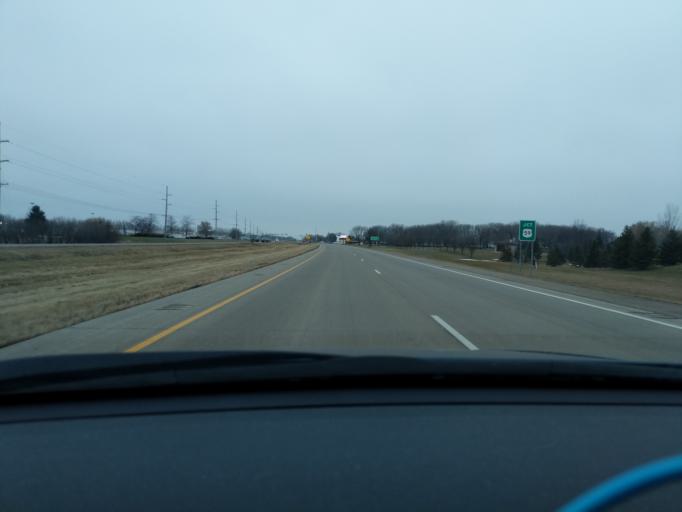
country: US
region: Minnesota
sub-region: Lyon County
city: Marshall
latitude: 44.4395
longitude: -95.7693
